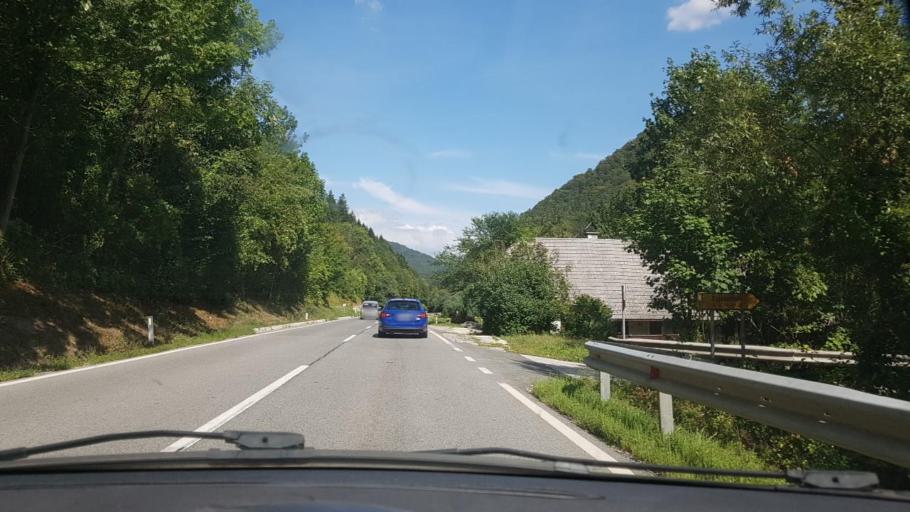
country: SI
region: Vransko
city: Vransko
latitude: 46.2137
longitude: 14.9212
